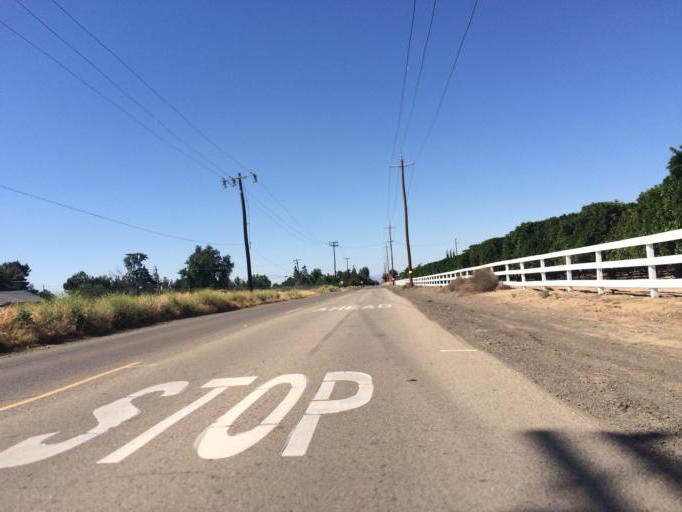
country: US
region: California
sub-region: Fresno County
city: Sanger
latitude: 36.7485
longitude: -119.6101
